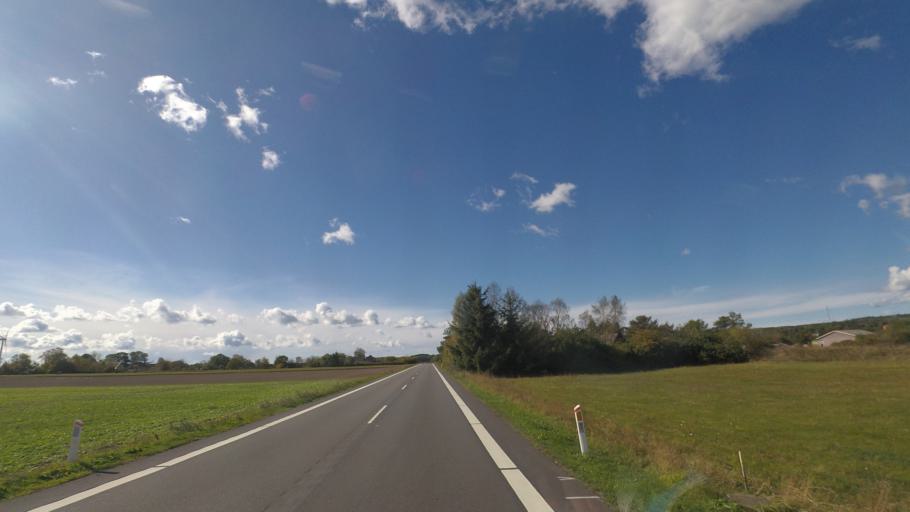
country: DK
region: Capital Region
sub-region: Bornholm Kommune
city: Nexo
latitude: 55.0608
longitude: 15.0559
